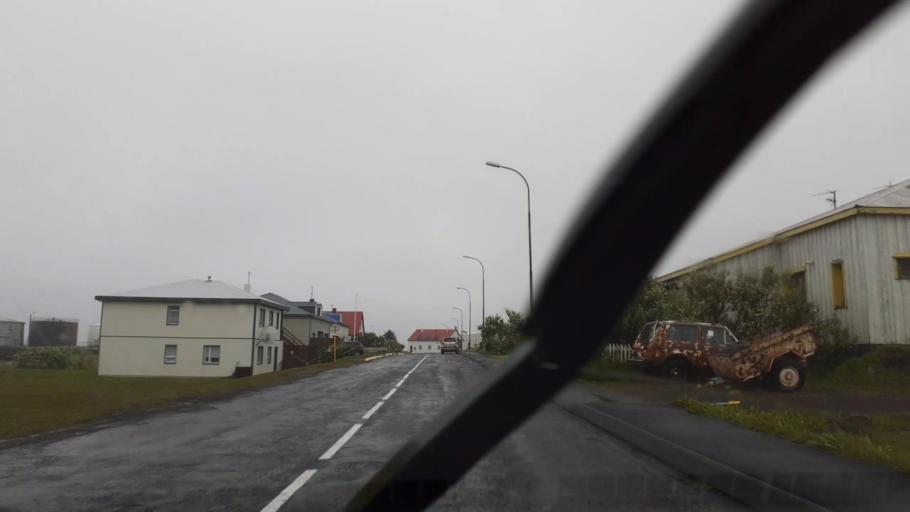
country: IS
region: Northeast
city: Husavik
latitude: 66.4558
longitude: -15.9546
